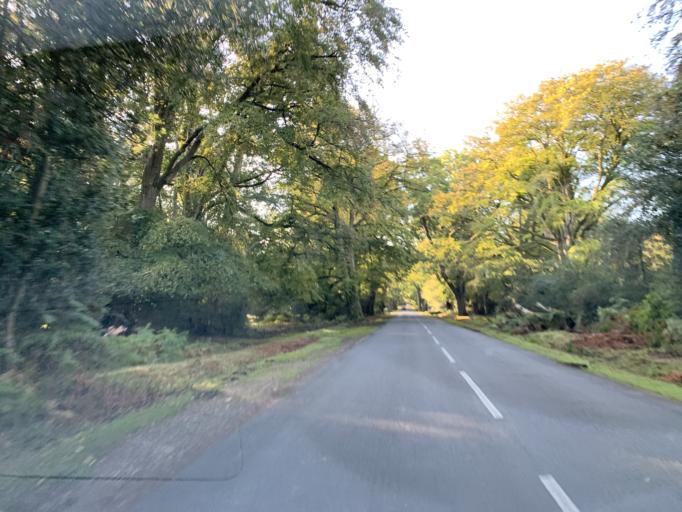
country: GB
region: England
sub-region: Hampshire
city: West Wellow
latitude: 50.9565
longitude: -1.6301
